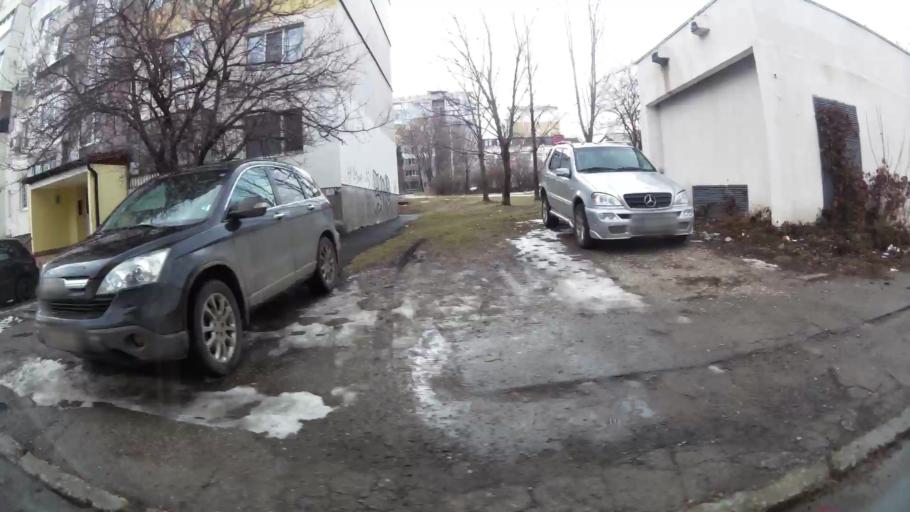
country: BG
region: Sofiya
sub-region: Obshtina Bozhurishte
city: Bozhurishte
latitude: 42.7199
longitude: 23.2453
